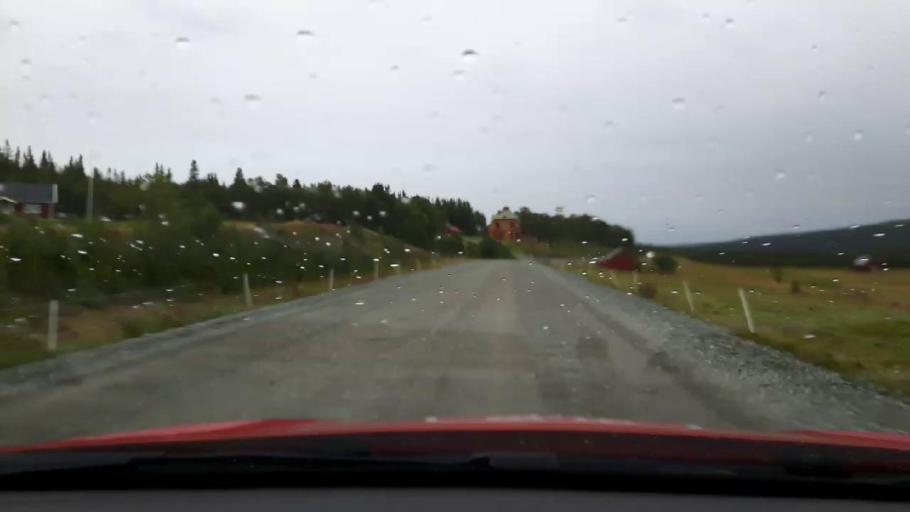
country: NO
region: Nord-Trondelag
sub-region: Meraker
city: Meraker
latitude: 63.5230
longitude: 12.4029
